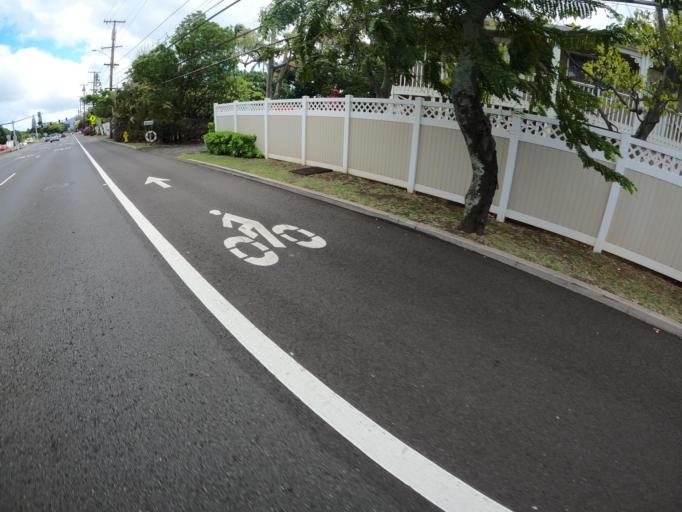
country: US
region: Hawaii
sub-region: Honolulu County
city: Waimanalo
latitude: 21.2760
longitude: -157.7647
